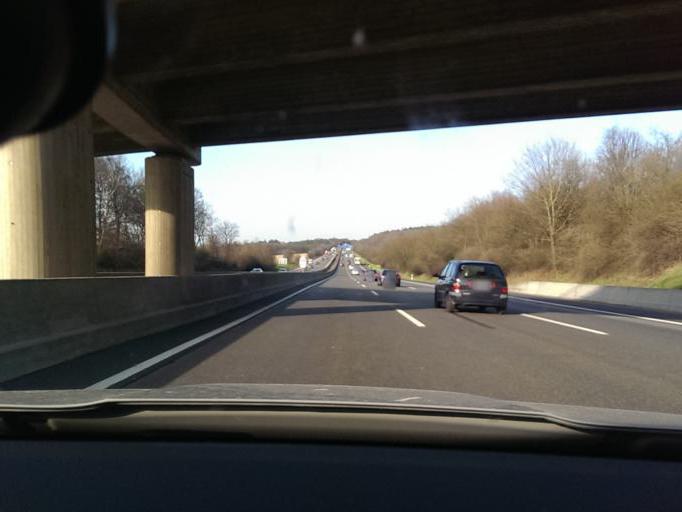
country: DE
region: Hesse
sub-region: Regierungsbezirk Kassel
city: Guxhagen
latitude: 51.2320
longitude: 9.4898
